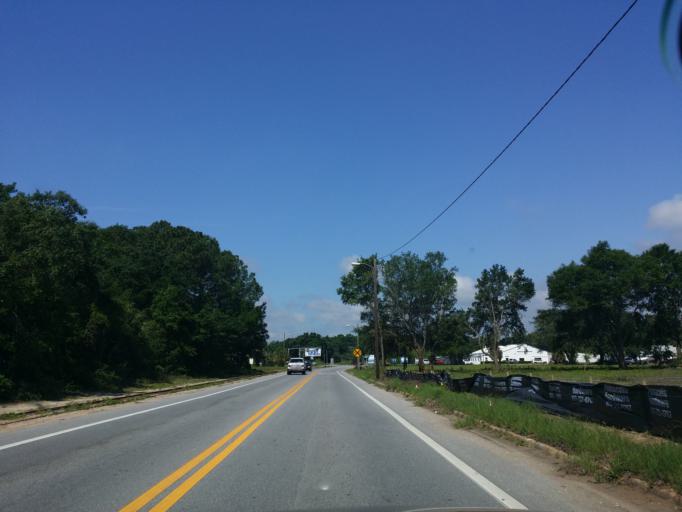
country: US
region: Florida
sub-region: Escambia County
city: Pensacola
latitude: 30.4058
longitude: -87.2354
